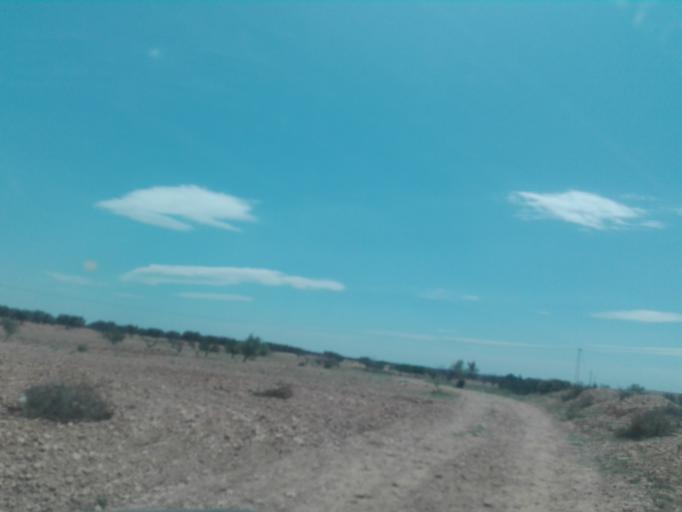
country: TN
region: Safaqis
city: Sfax
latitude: 34.6546
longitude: 10.5935
